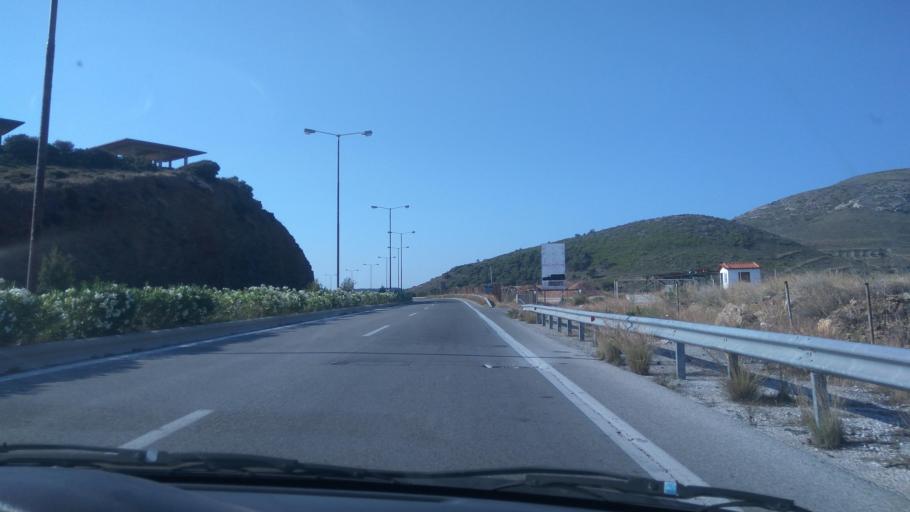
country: GR
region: Attica
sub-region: Nomarchia Anatolikis Attikis
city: Keratea
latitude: 37.7996
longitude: 24.0491
